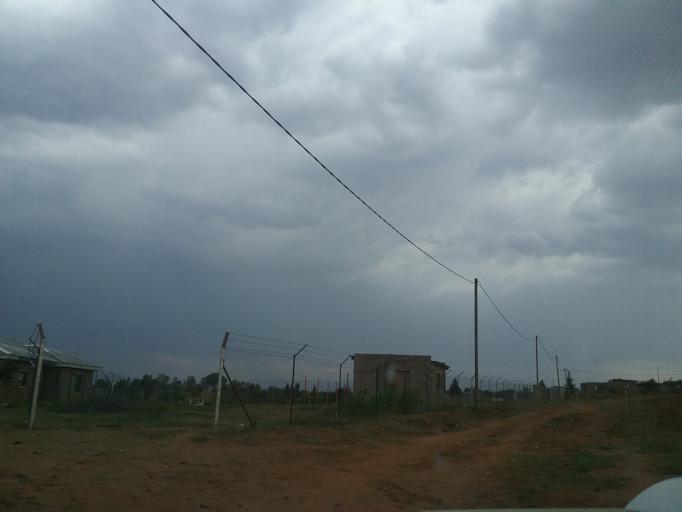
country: LS
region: Maseru
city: Maseru
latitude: -29.4186
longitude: 27.5677
